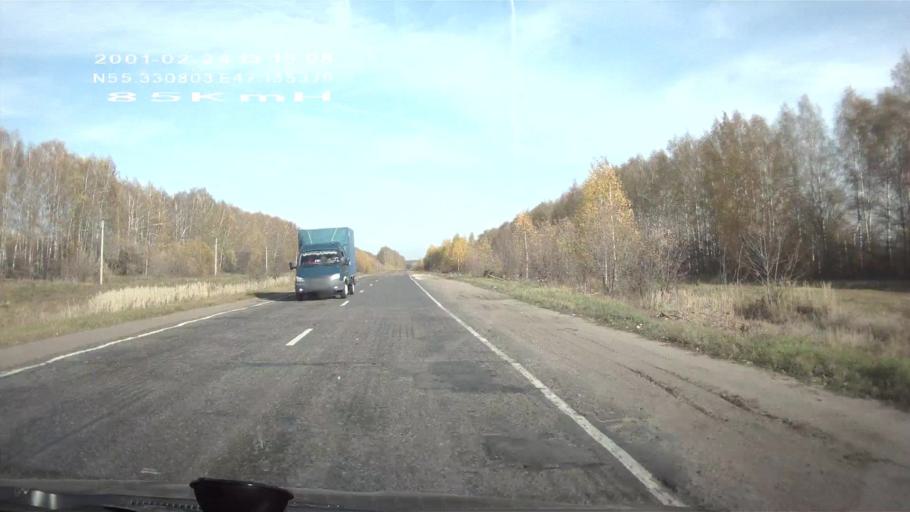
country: RU
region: Chuvashia
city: Ibresi
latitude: 55.3308
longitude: 47.1354
